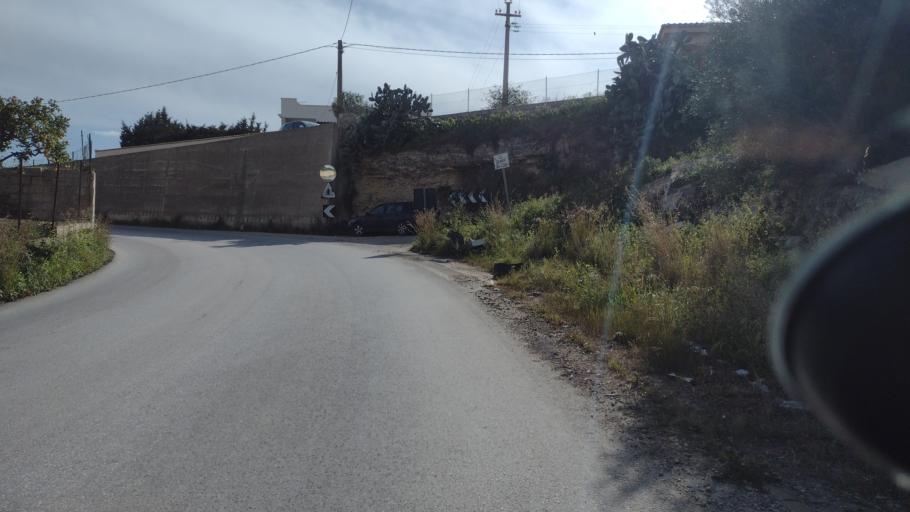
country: IT
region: Sicily
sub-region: Provincia di Siracusa
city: Avola
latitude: 36.8743
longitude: 15.1264
